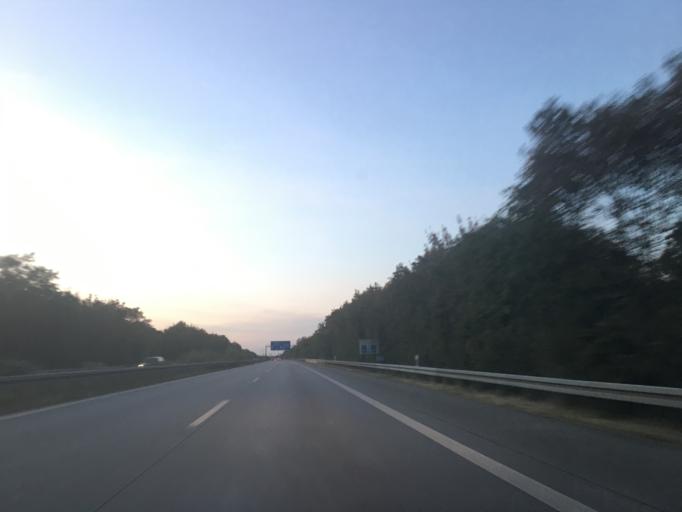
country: DE
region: Baden-Wuerttemberg
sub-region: Karlsruhe Region
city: Hockenheim
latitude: 49.3453
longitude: 8.5546
